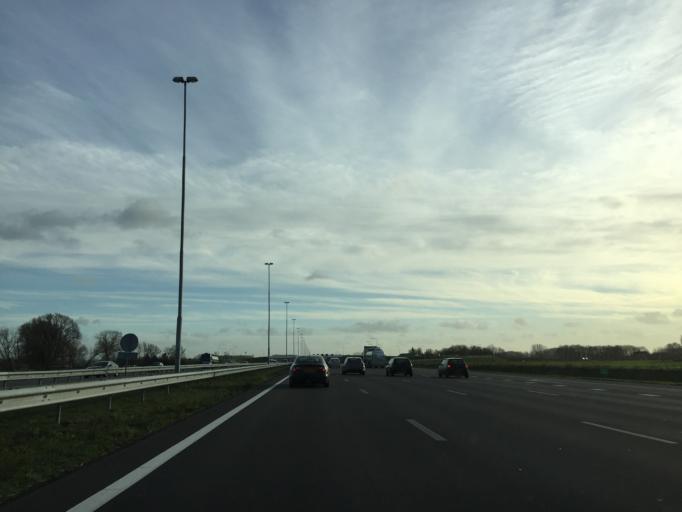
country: NL
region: Gelderland
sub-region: Gemeente Culemborg
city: Culemborg
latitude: 51.9335
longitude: 5.1596
